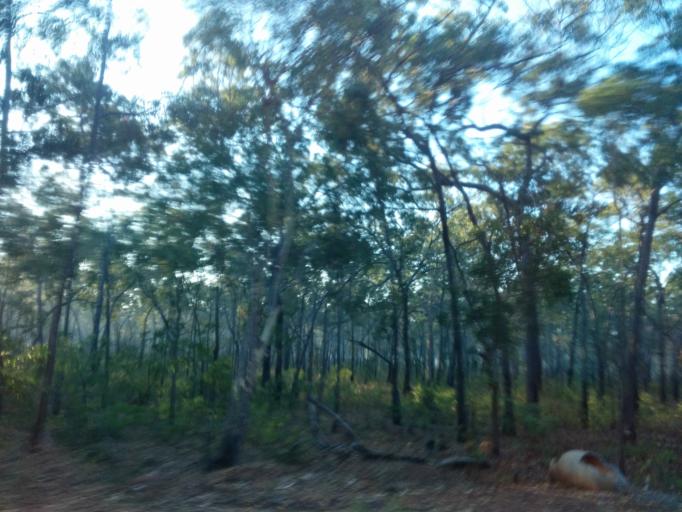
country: AU
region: Northern Territory
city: Alyangula
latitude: -13.8652
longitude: 136.8044
